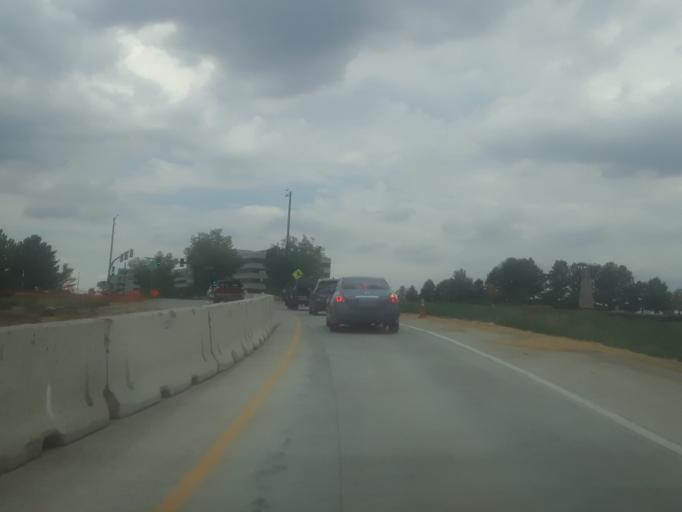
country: US
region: Colorado
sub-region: Douglas County
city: Highlands Ranch
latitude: 39.5590
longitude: -105.0094
